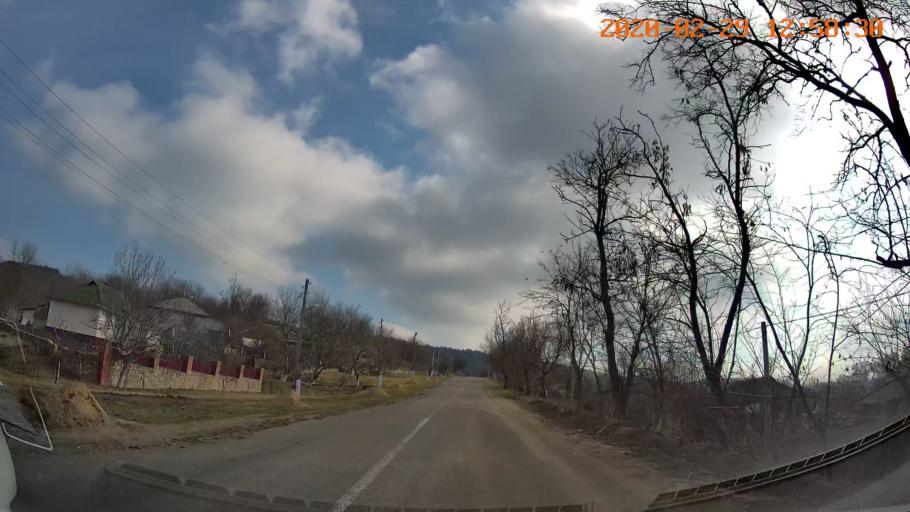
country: MD
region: Telenesti
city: Camenca
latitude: 48.0699
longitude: 28.7215
